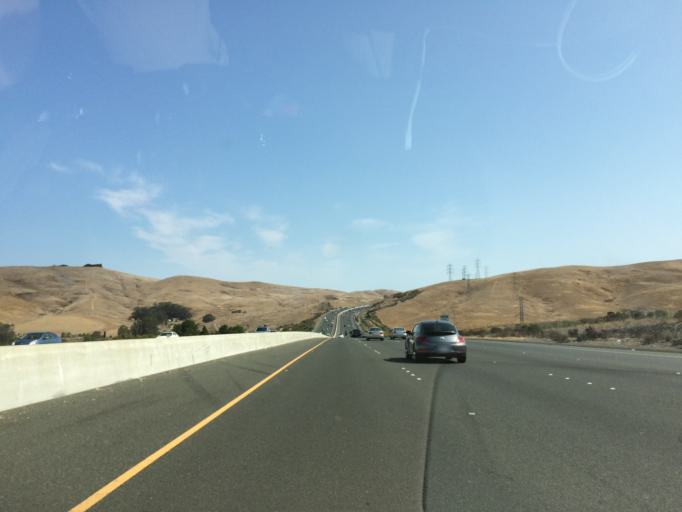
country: US
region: California
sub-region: Napa County
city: American Canyon
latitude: 38.1555
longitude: -122.2144
